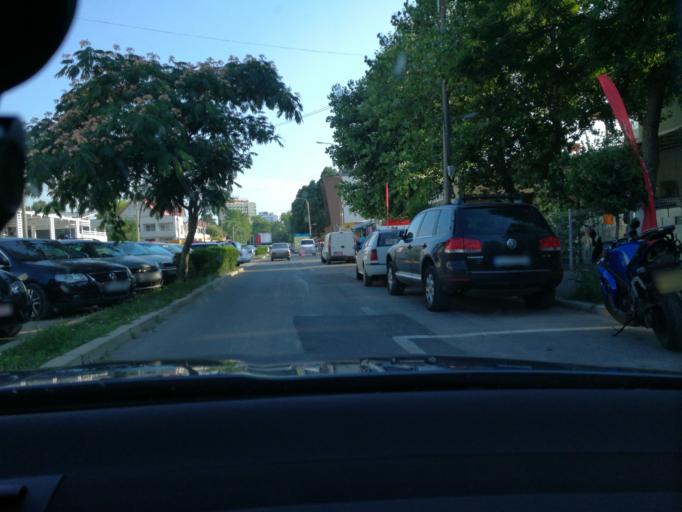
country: RO
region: Constanta
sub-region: Oras Eforie
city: Eforie Nord
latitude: 44.0703
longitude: 28.6380
